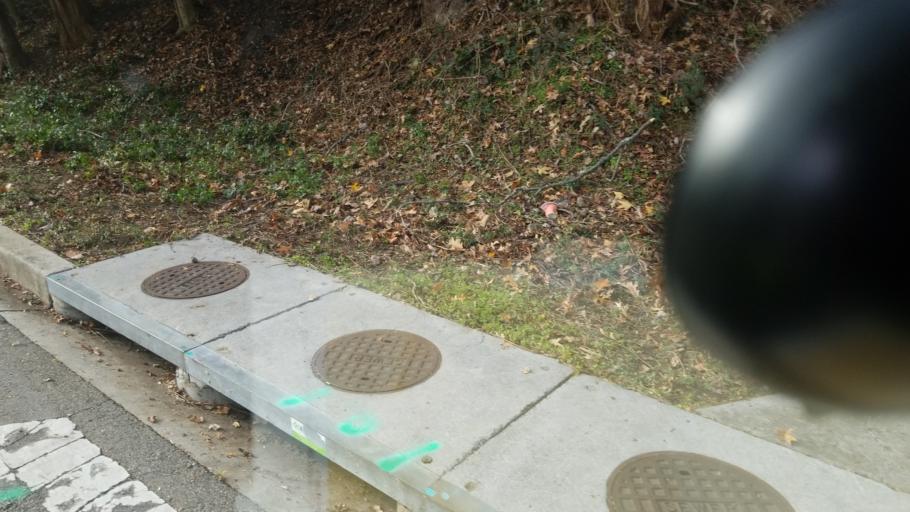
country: US
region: Maryland
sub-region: Prince George's County
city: Silver Hill
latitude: 38.8766
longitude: -76.9576
